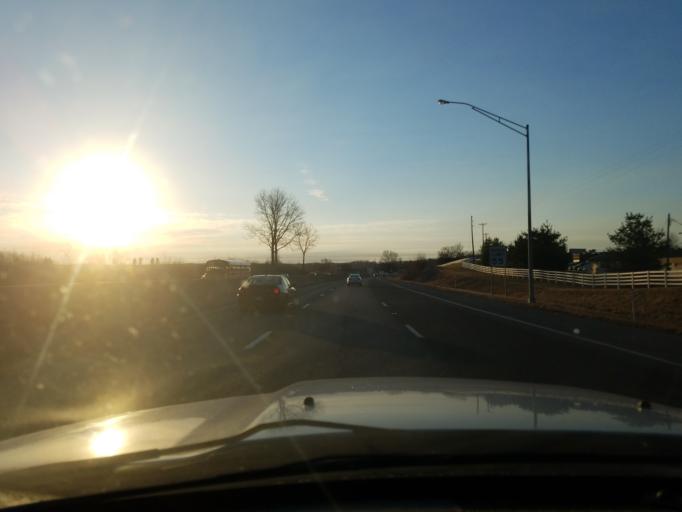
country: US
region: Kentucky
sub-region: Henderson County
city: Henderson
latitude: 37.8544
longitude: -87.5703
